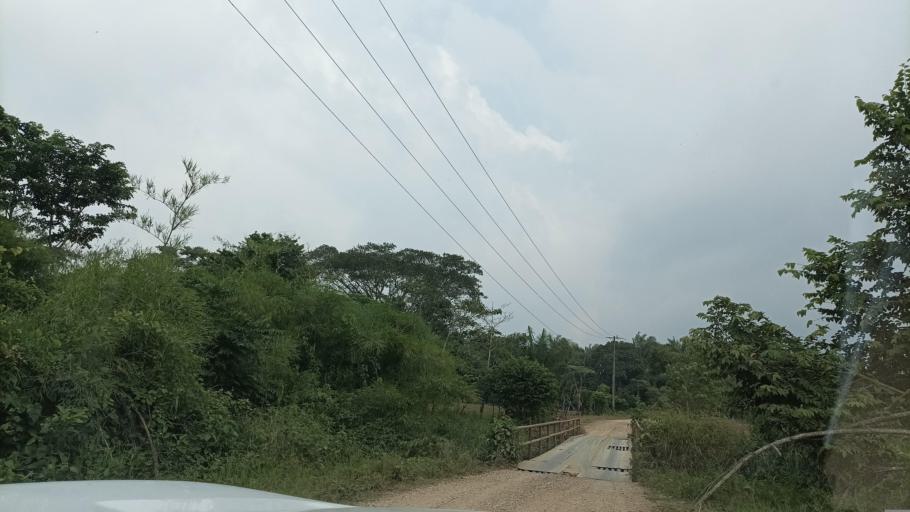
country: MX
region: Veracruz
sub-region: Moloacan
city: Cuichapa
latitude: 17.5864
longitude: -94.2061
